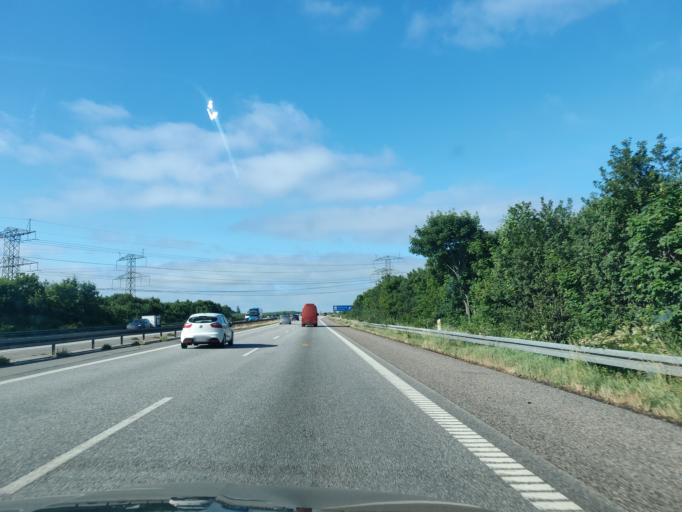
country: DK
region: North Denmark
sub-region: Alborg Kommune
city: Svenstrup
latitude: 56.9560
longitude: 9.8703
